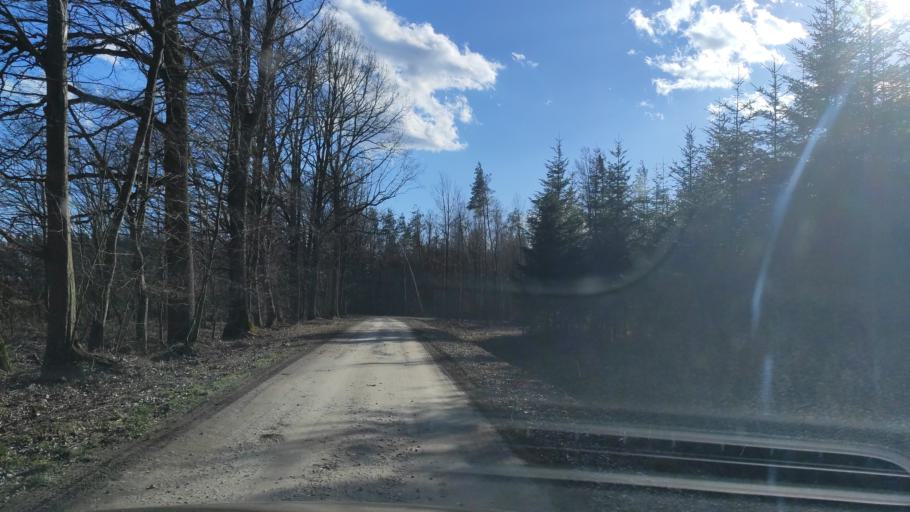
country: PL
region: Masovian Voivodeship
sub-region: Powiat radomski
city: Jedlnia-Letnisko
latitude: 51.4467
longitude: 21.2949
